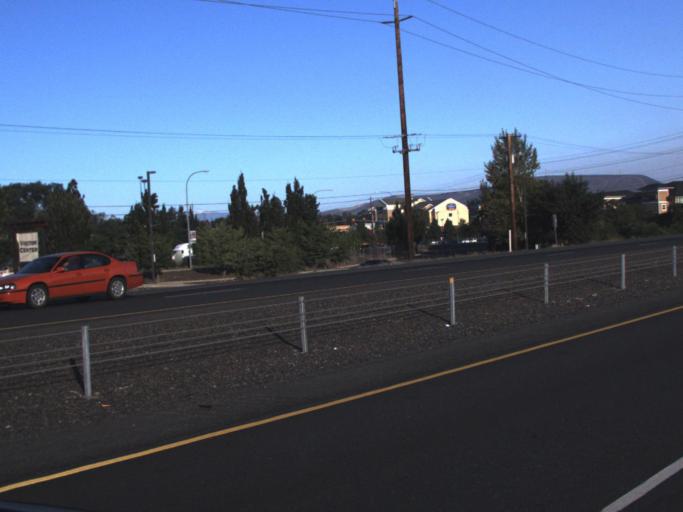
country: US
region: Washington
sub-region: Yakima County
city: Yakima
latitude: 46.6076
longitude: -120.4877
